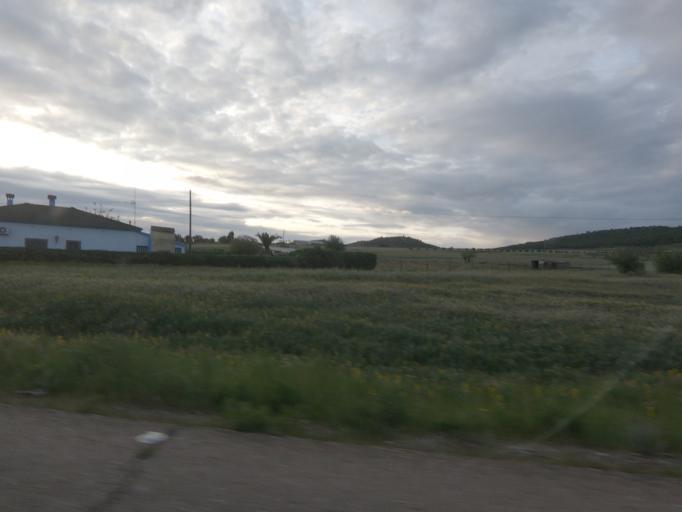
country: ES
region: Extremadura
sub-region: Provincia de Badajoz
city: Puebla de Obando
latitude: 39.1770
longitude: -6.6177
